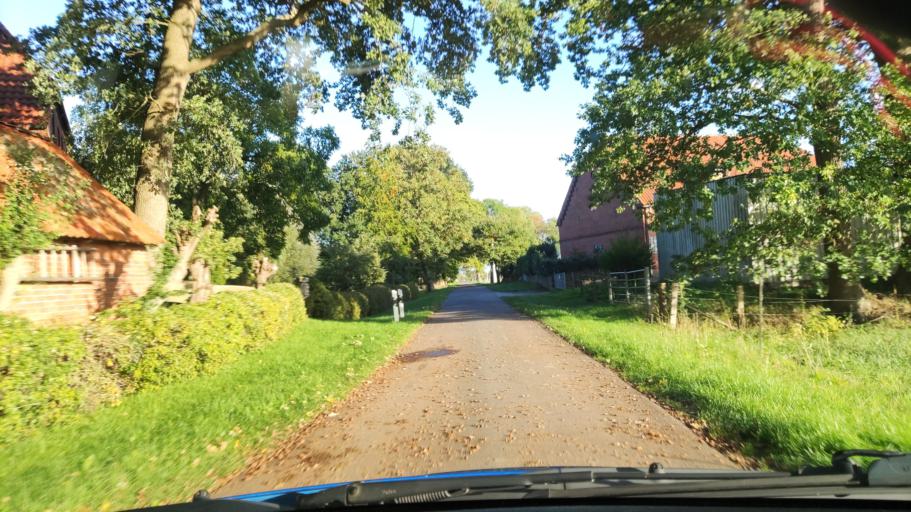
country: DE
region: Lower Saxony
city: Bleckede
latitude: 53.3211
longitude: 10.7919
